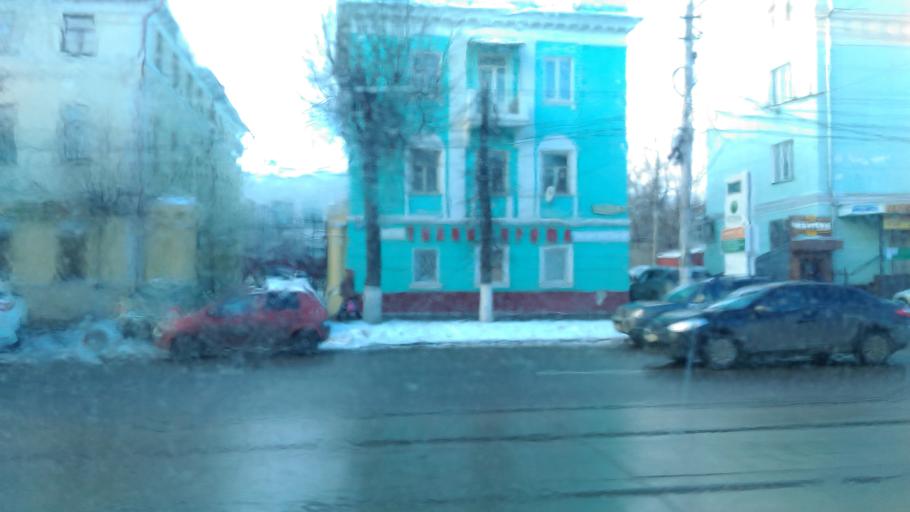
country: RU
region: Tula
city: Tula
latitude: 54.2071
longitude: 37.6196
